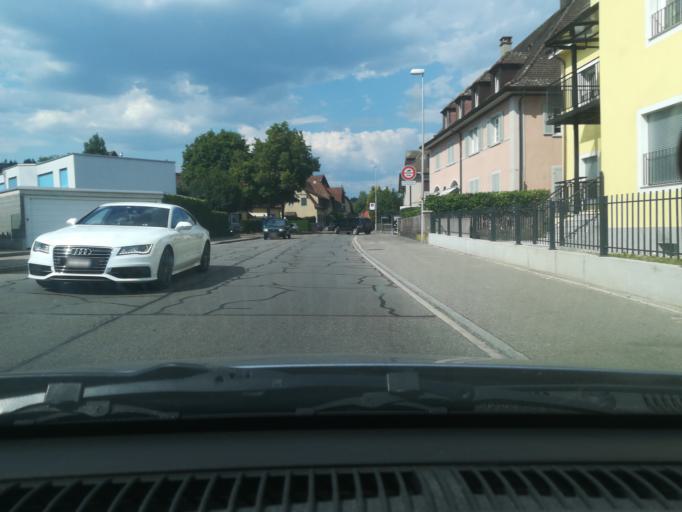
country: CH
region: Schaffhausen
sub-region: Bezirk Schaffhausen
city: Schaffhausen
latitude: 47.7082
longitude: 8.6279
